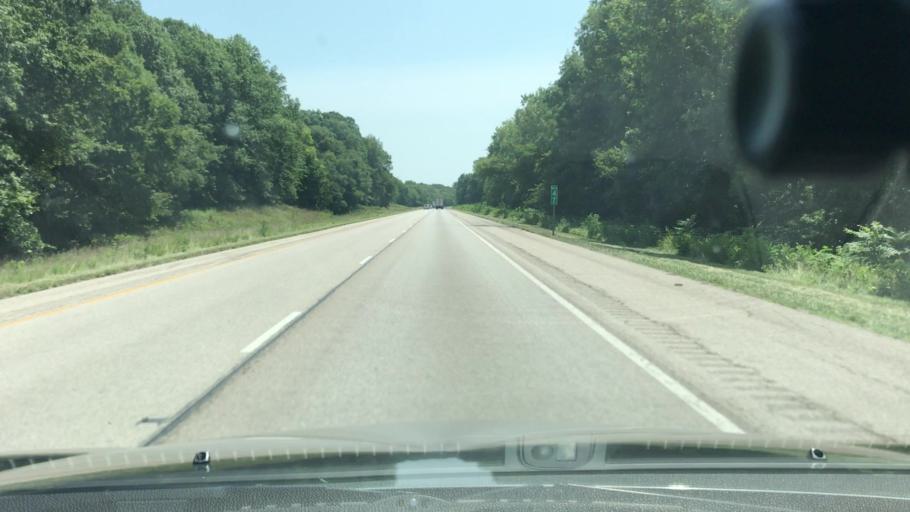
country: US
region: Illinois
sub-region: Washington County
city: Nashville
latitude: 38.4092
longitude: -89.4208
